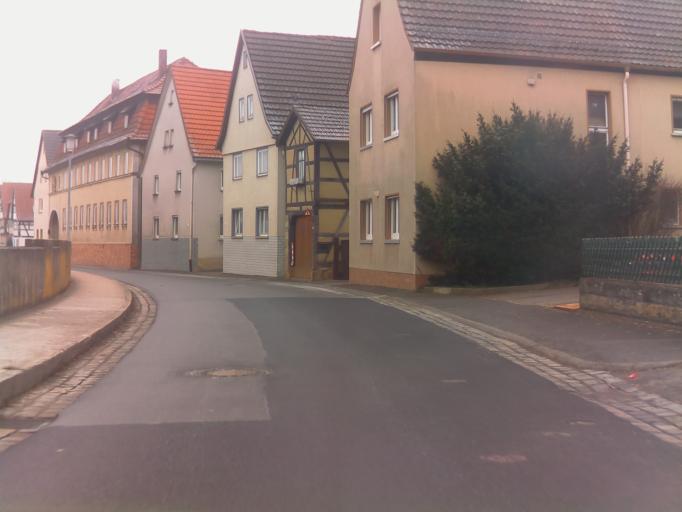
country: DE
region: Bavaria
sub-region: Regierungsbezirk Unterfranken
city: Sondheim vor der Rhoen
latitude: 50.4781
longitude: 10.1826
